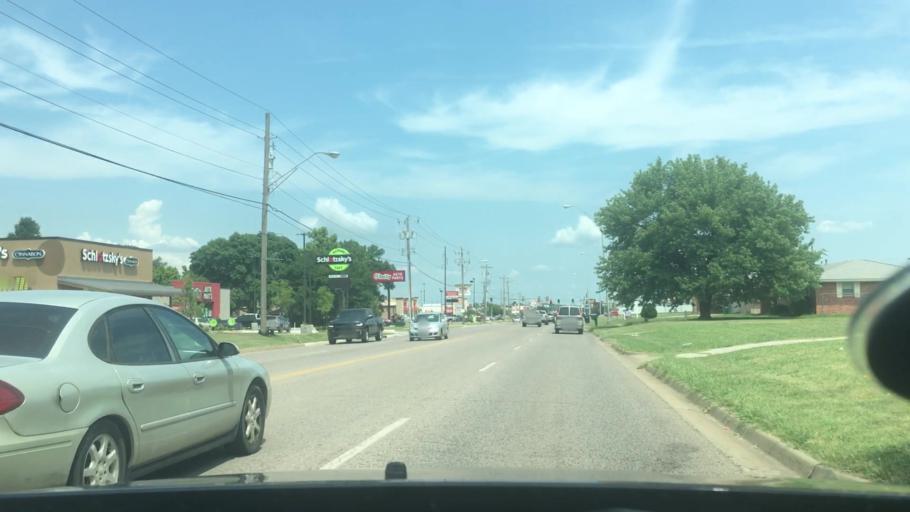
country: US
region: Oklahoma
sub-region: Pottawatomie County
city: Shawnee
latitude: 35.3738
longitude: -96.9297
